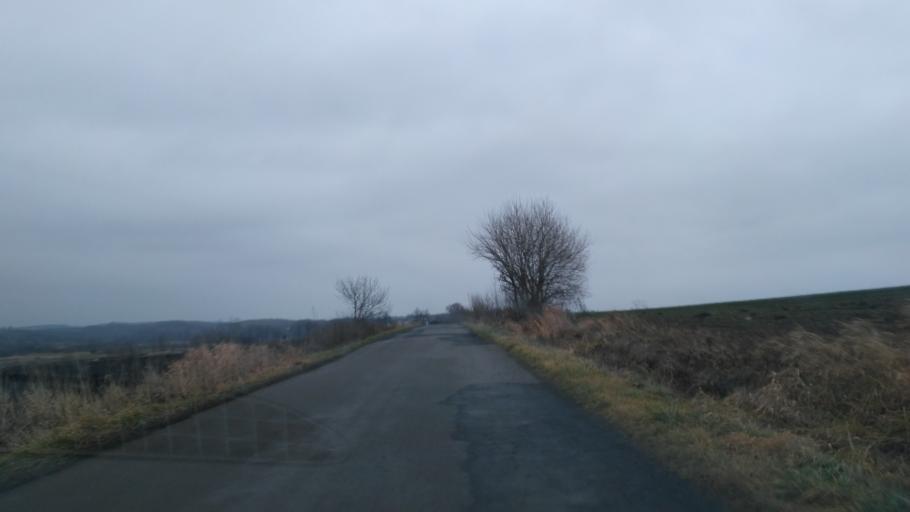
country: PL
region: Subcarpathian Voivodeship
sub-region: Powiat jaroslawski
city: Pruchnik
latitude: 49.9360
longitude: 22.5472
